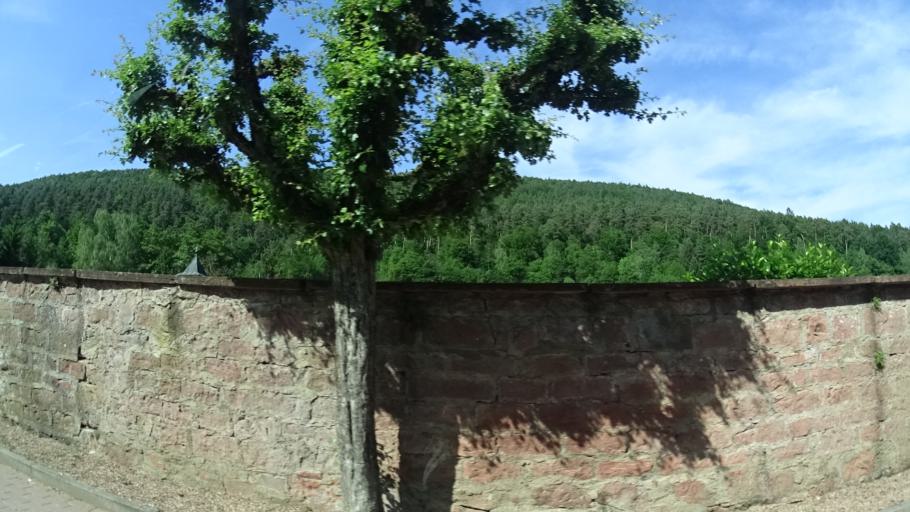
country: DE
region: Bavaria
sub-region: Regierungsbezirk Unterfranken
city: Weilbach
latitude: 49.6748
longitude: 9.1804
